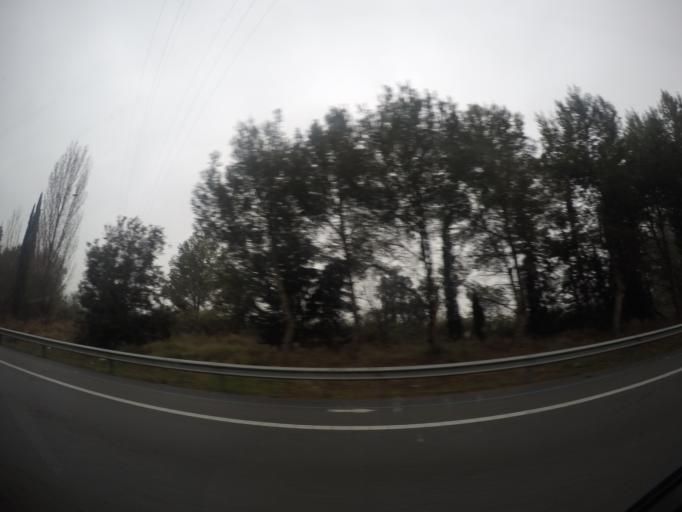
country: ES
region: Catalonia
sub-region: Provincia de Barcelona
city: Subirats
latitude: 41.4269
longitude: 1.8327
